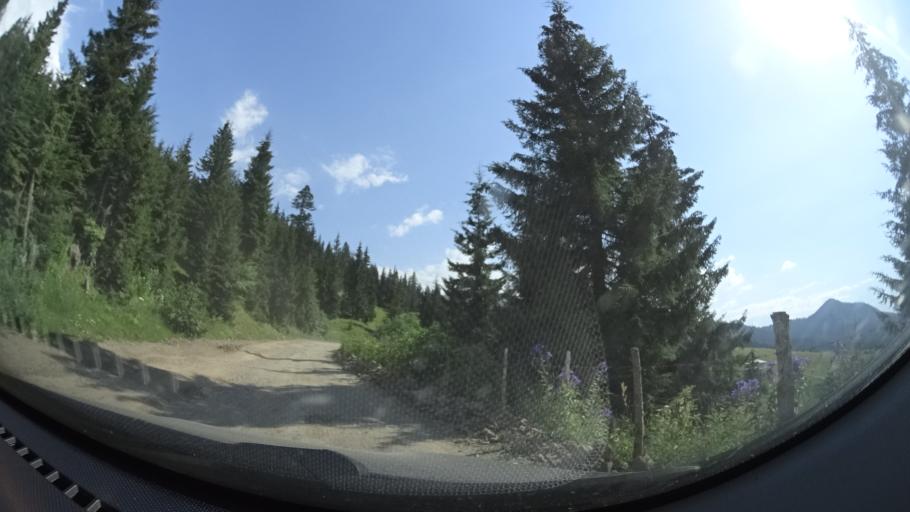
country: GE
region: Ajaria
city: Dioknisi
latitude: 41.6345
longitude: 42.4941
